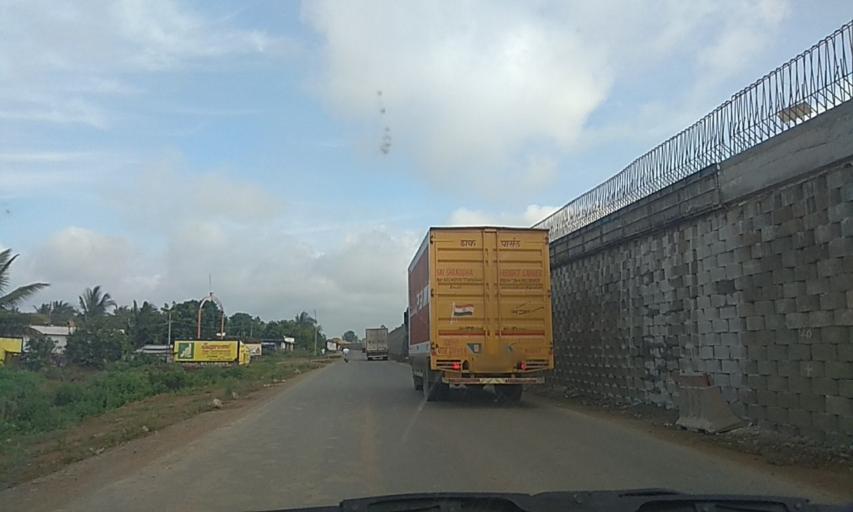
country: IN
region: Karnataka
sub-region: Haveri
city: Savanur
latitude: 14.8702
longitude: 75.3188
